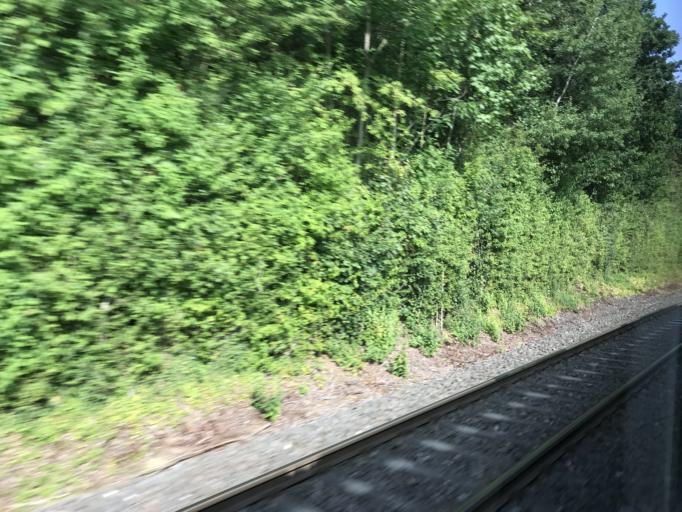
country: DE
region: Hesse
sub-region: Regierungsbezirk Giessen
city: Runkel
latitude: 50.3818
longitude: 8.1329
